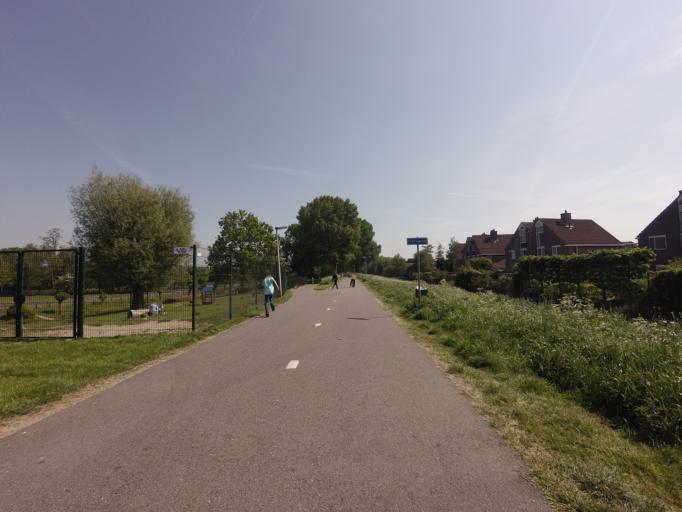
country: NL
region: South Holland
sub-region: Gemeente Hellevoetsluis
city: Hellevoetsluis
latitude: 51.8294
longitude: 4.1539
